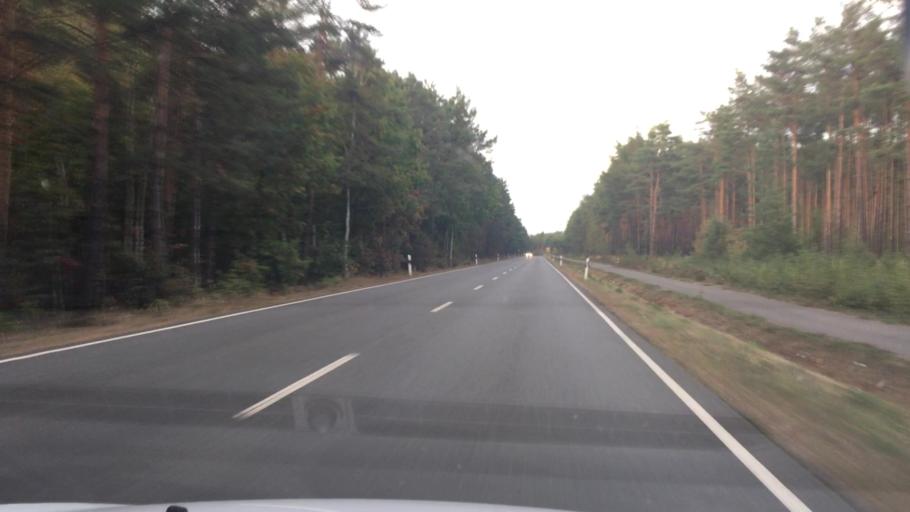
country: DE
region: Brandenburg
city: Schipkau
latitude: 51.4983
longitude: 13.8964
